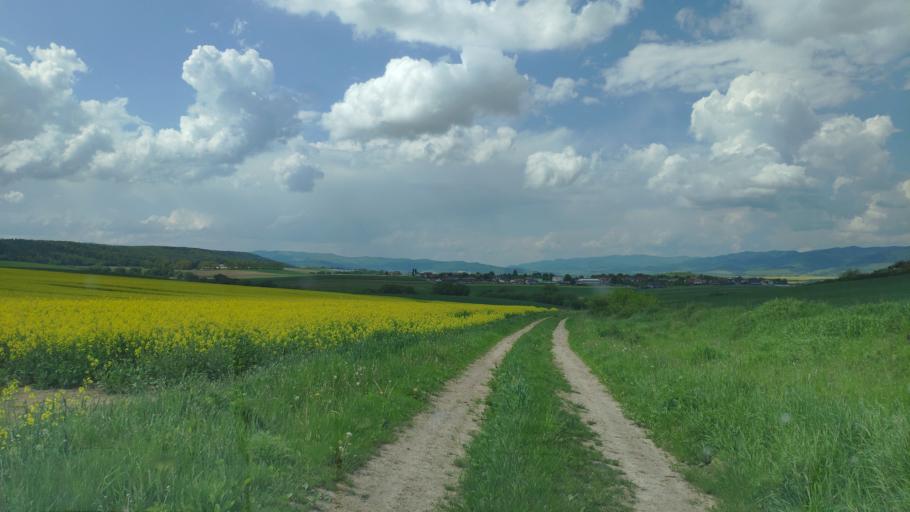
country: SK
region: Presovsky
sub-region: Okres Presov
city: Presov
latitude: 49.0309
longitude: 21.1665
